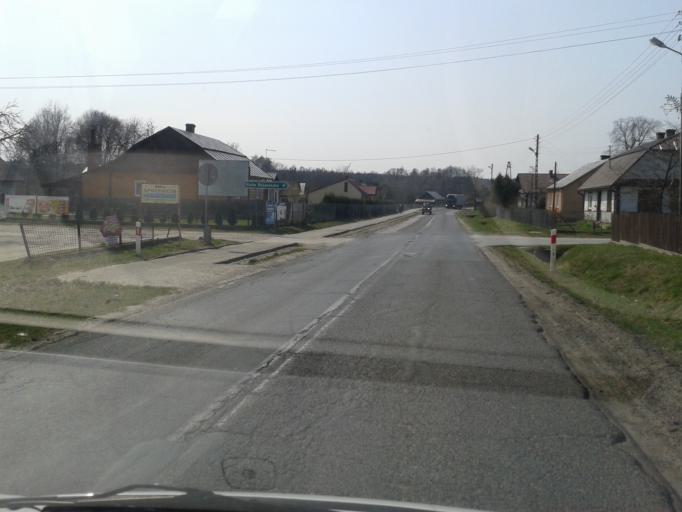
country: PL
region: Subcarpathian Voivodeship
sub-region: Powiat lubaczowski
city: Narol
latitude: 50.3135
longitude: 23.2439
